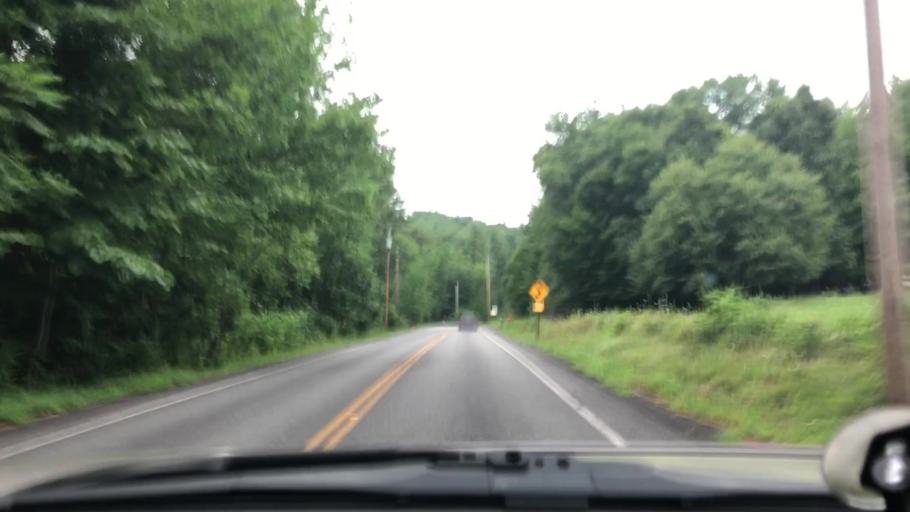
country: US
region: New York
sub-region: Saratoga County
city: Corinth
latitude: 43.1872
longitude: -73.7514
